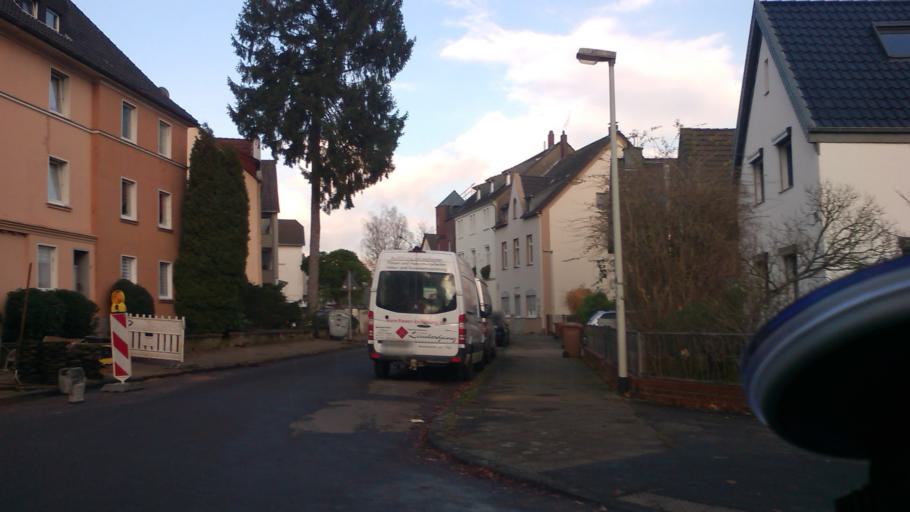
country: DE
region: North Rhine-Westphalia
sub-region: Regierungsbezirk Dusseldorf
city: Hilden
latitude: 51.1603
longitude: 6.9352
